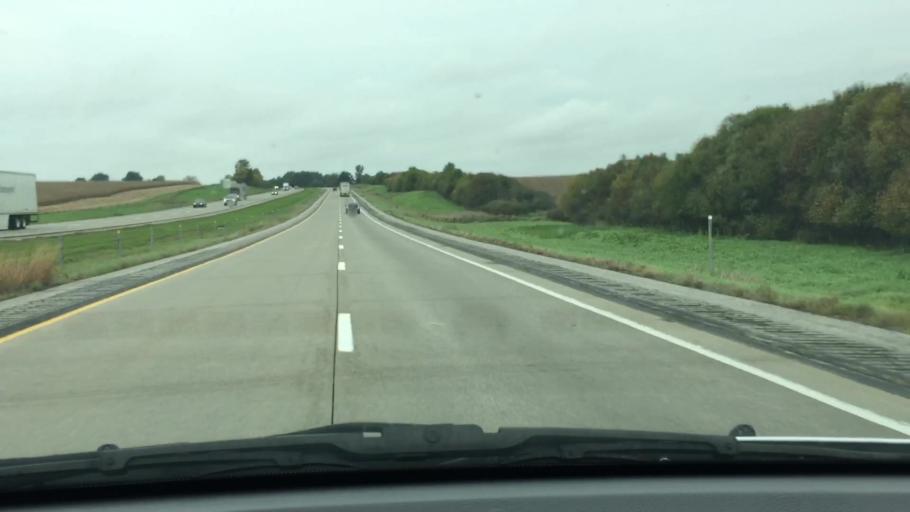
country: US
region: Iowa
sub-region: Cedar County
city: West Branch
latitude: 41.6664
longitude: -91.3672
